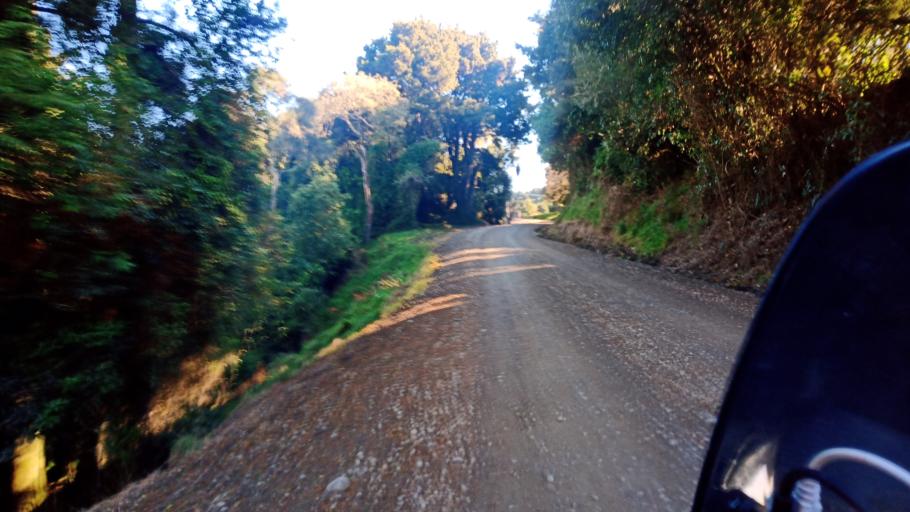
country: NZ
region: Hawke's Bay
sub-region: Wairoa District
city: Wairoa
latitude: -38.8160
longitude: 177.2913
